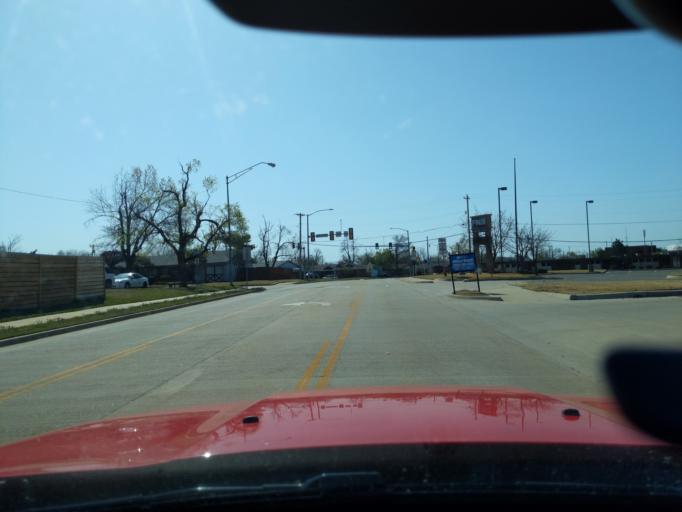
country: US
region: Oklahoma
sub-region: Cleveland County
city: Moore
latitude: 35.3442
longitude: -97.4875
